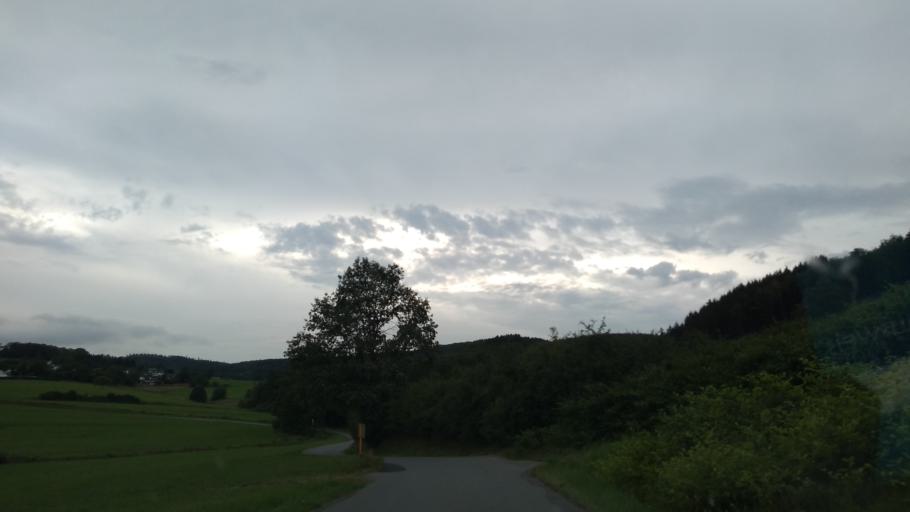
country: DE
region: North Rhine-Westphalia
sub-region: Regierungsbezirk Arnsberg
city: Herscheid
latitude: 51.1938
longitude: 7.7862
